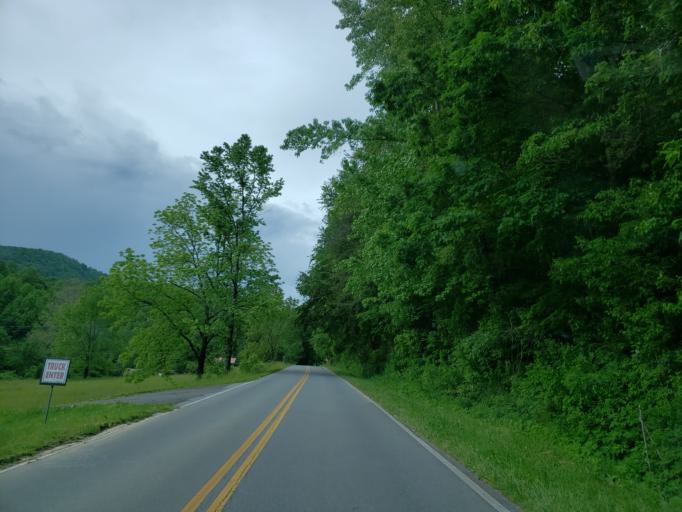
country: US
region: Georgia
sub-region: Fannin County
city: Blue Ridge
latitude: 34.8310
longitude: -84.4049
